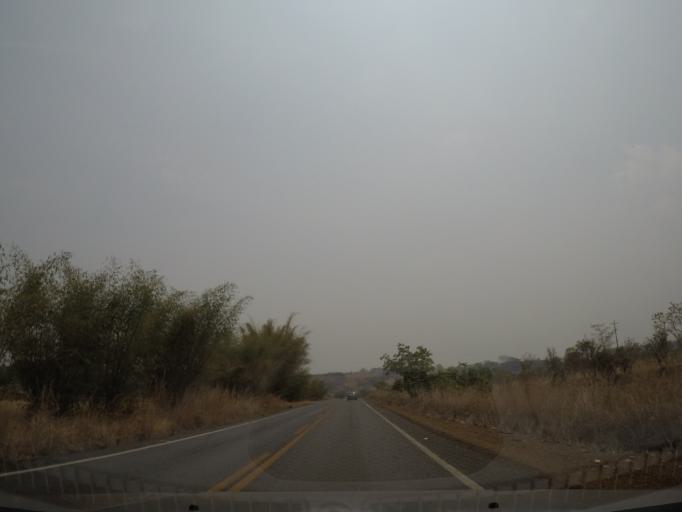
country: BR
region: Goias
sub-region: Pirenopolis
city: Pirenopolis
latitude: -15.8906
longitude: -48.8928
